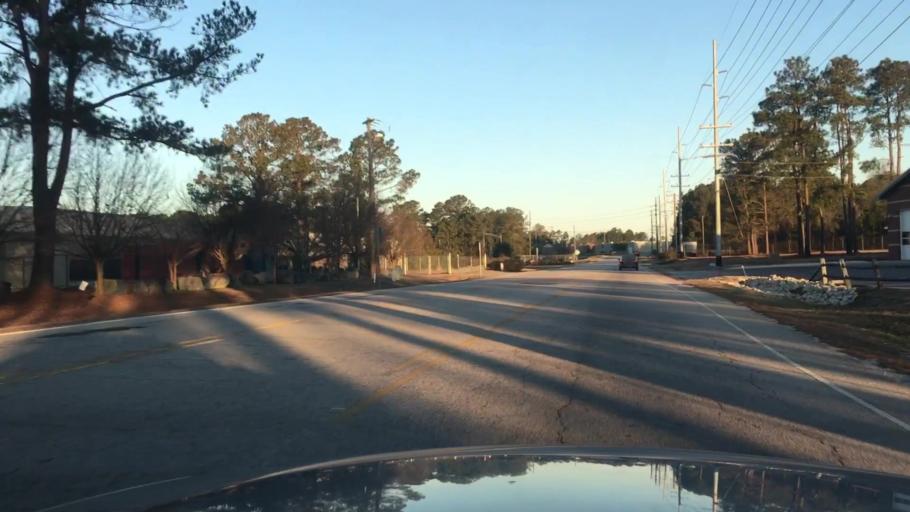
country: US
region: North Carolina
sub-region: Cumberland County
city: Hope Mills
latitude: 34.9974
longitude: -78.9027
